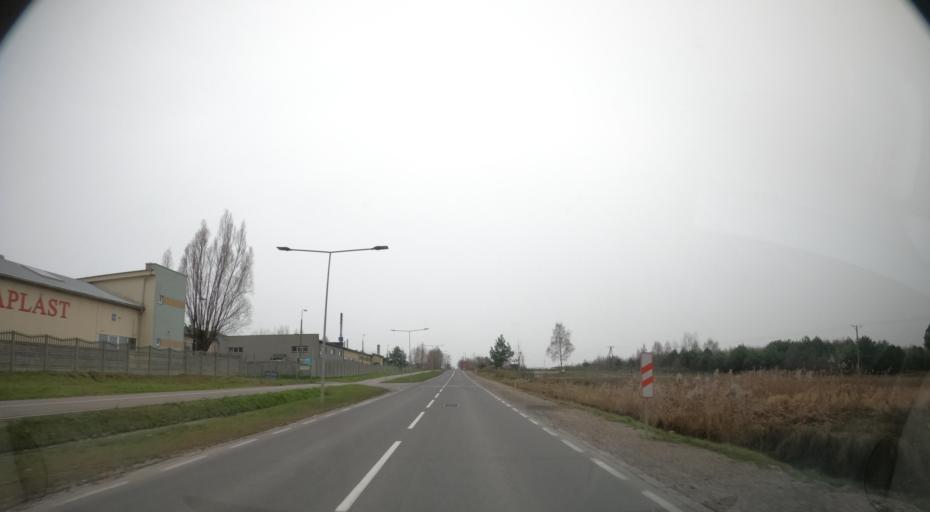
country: PL
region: Masovian Voivodeship
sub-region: Radom
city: Radom
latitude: 51.4429
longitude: 21.1903
